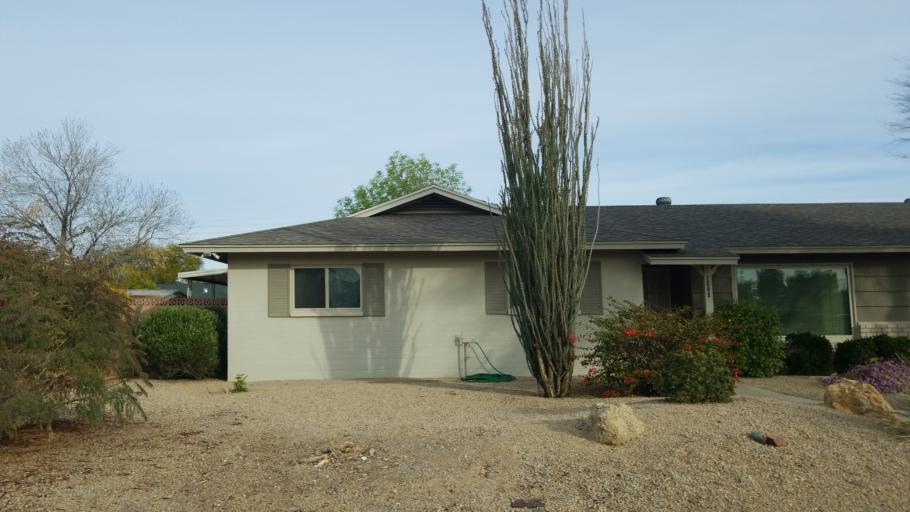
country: US
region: Arizona
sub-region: Maricopa County
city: Phoenix
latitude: 33.5340
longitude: -112.0933
